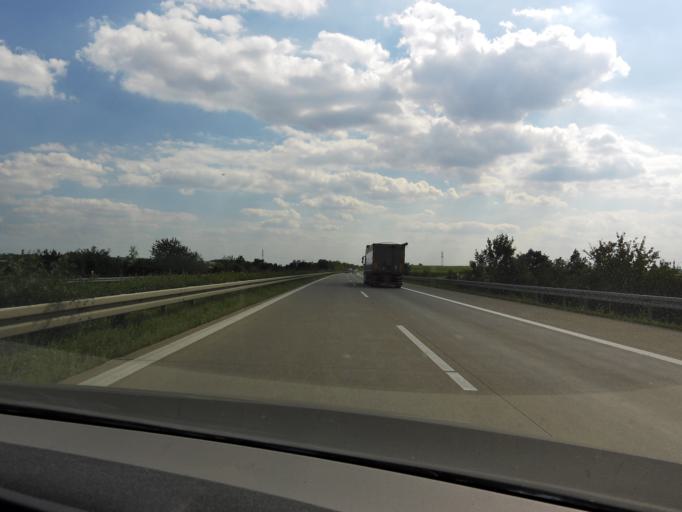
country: DE
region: Saxony-Anhalt
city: Eickendorf
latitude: 51.9303
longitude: 11.6983
